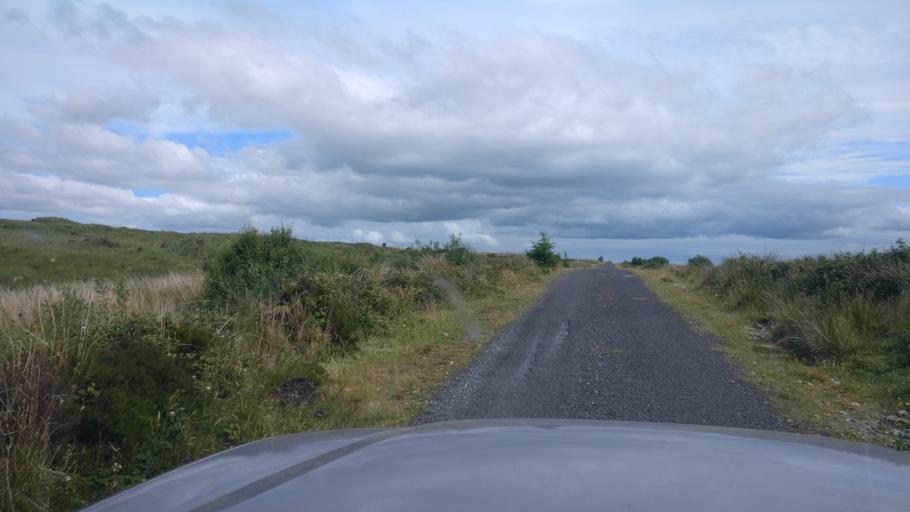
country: IE
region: Connaught
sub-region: County Galway
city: Gort
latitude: 53.0810
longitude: -8.6870
